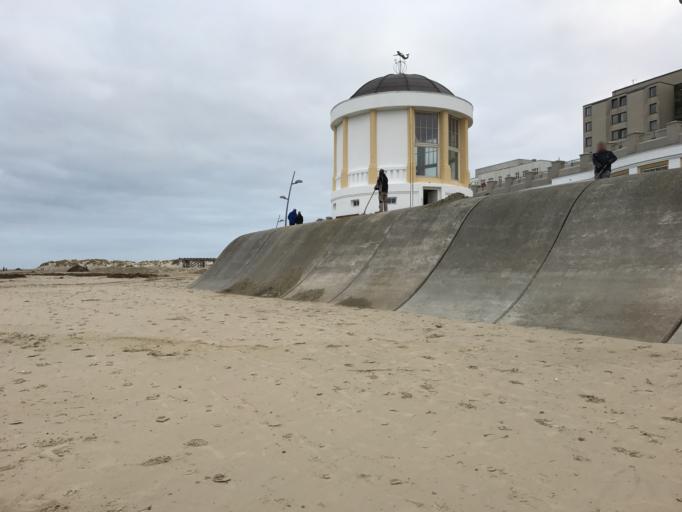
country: DE
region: Lower Saxony
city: Borkum
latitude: 53.5884
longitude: 6.6569
